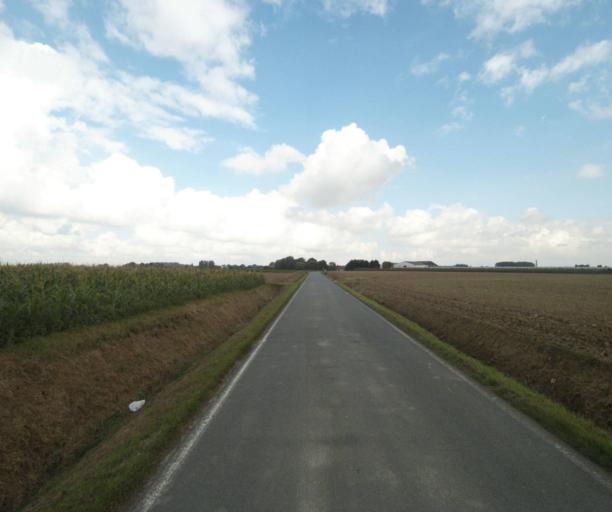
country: FR
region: Nord-Pas-de-Calais
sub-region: Departement du Nord
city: Herlies
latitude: 50.5958
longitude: 2.8518
